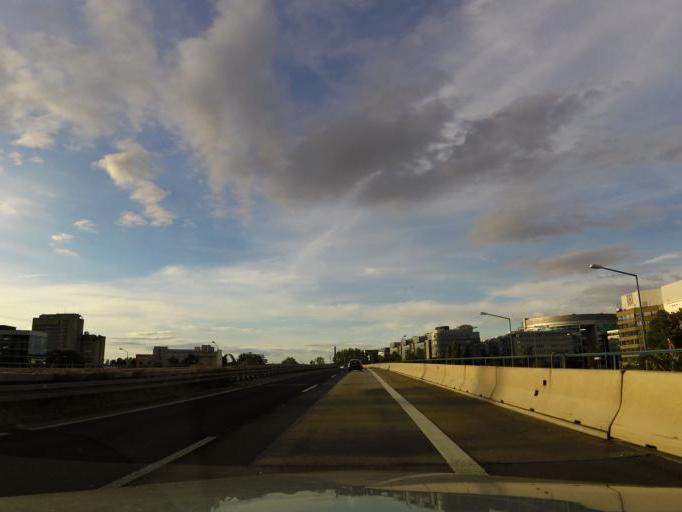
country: DE
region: Hesse
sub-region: Regierungsbezirk Darmstadt
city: Offenbach
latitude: 50.1046
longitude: 8.7386
